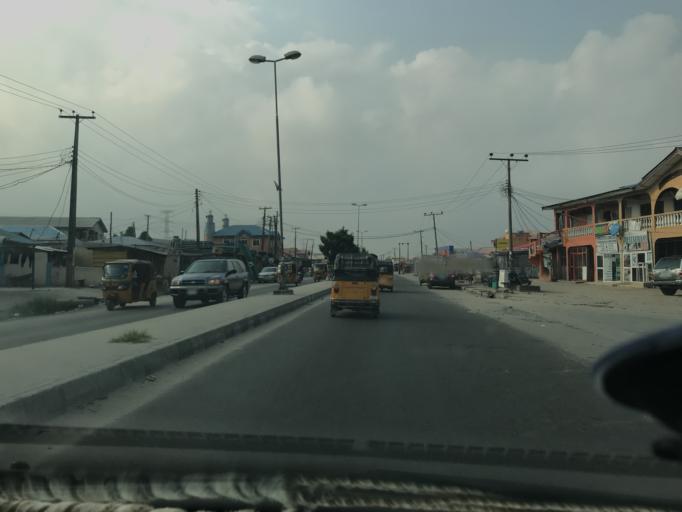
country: NG
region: Lagos
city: Ebute Ikorodu
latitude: 6.4936
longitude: 3.5825
